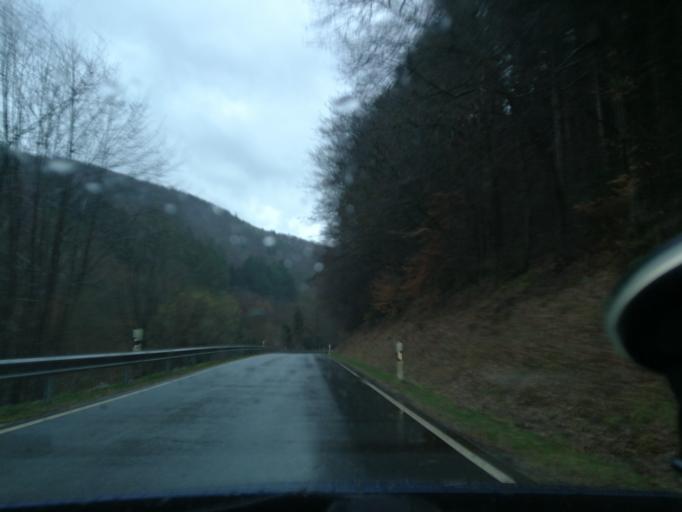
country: DE
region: Rheinland-Pfalz
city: Heidenburg
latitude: 49.8260
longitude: 6.9469
